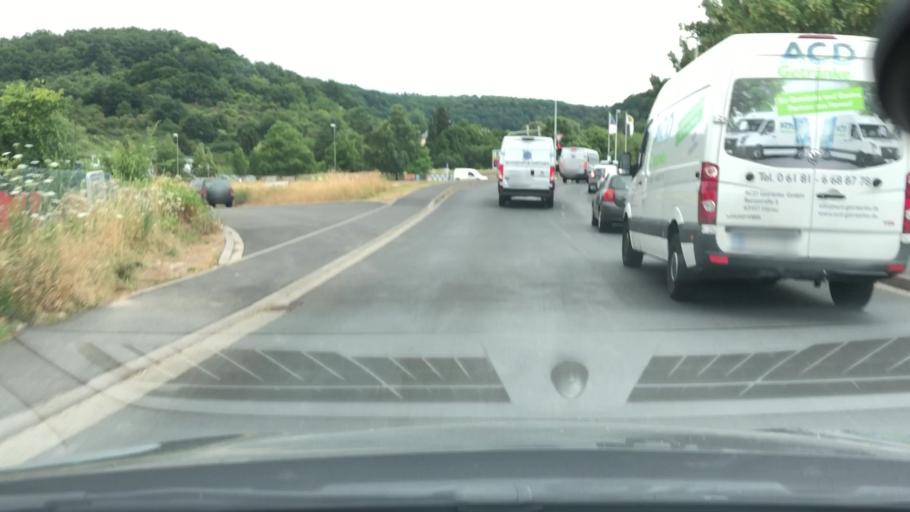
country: DE
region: Hesse
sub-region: Regierungsbezirk Darmstadt
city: Gelnhausen
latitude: 50.2044
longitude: 9.1717
